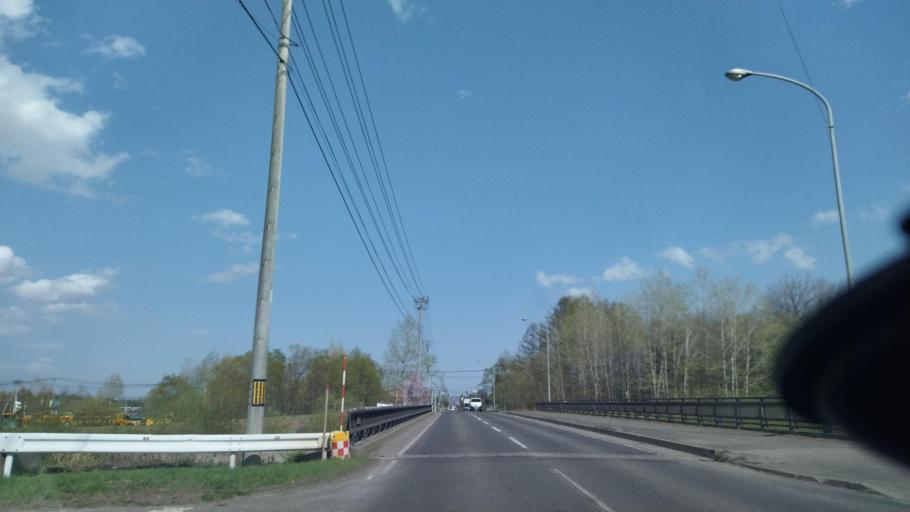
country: JP
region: Hokkaido
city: Obihiro
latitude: 42.9325
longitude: 143.1400
